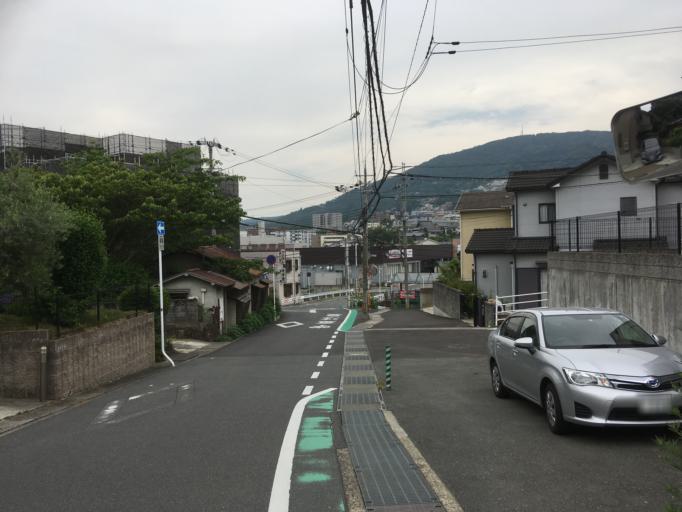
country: JP
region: Nara
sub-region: Ikoma-shi
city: Ikoma
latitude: 34.6969
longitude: 135.7028
